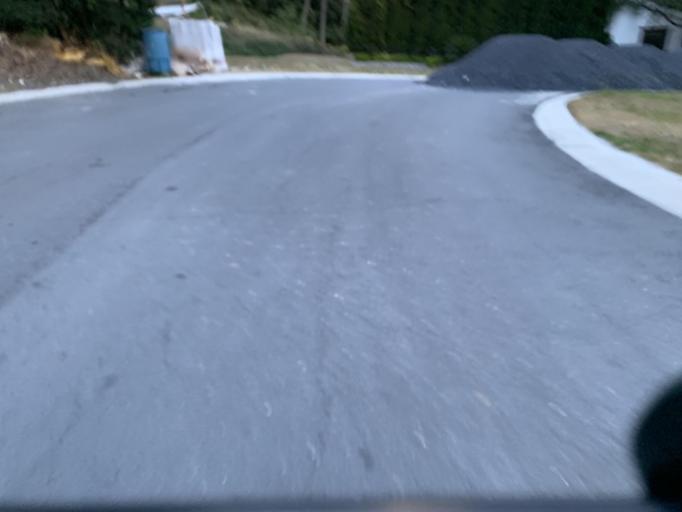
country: MX
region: Nuevo Leon
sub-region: Juarez
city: Bosques de San Pedro
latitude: 25.5232
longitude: -100.1915
